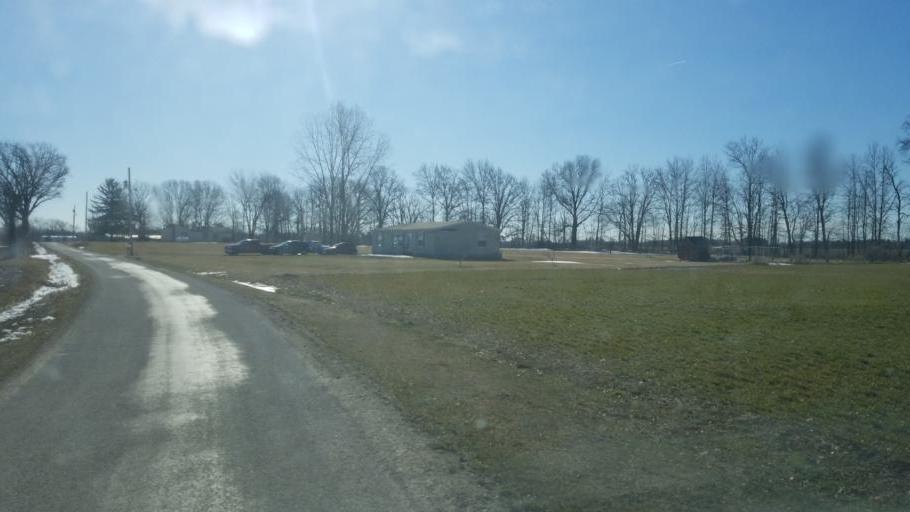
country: US
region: Ohio
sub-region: Morrow County
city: Mount Gilead
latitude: 40.6617
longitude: -82.9178
